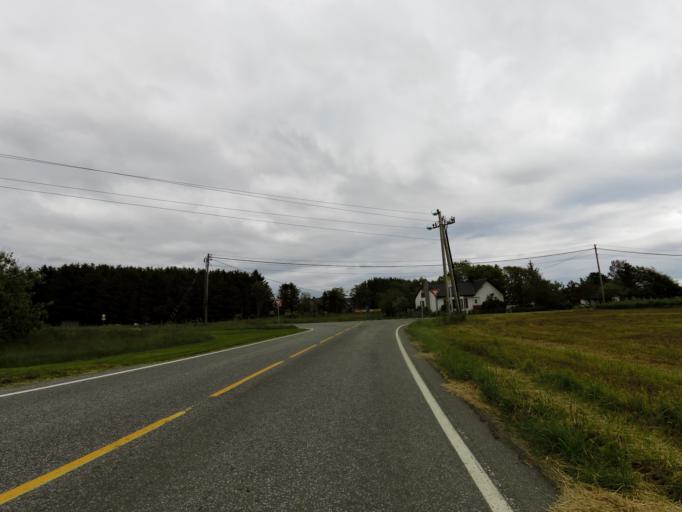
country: NO
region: Vest-Agder
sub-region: Farsund
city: Vestbygd
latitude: 58.1163
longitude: 6.6048
